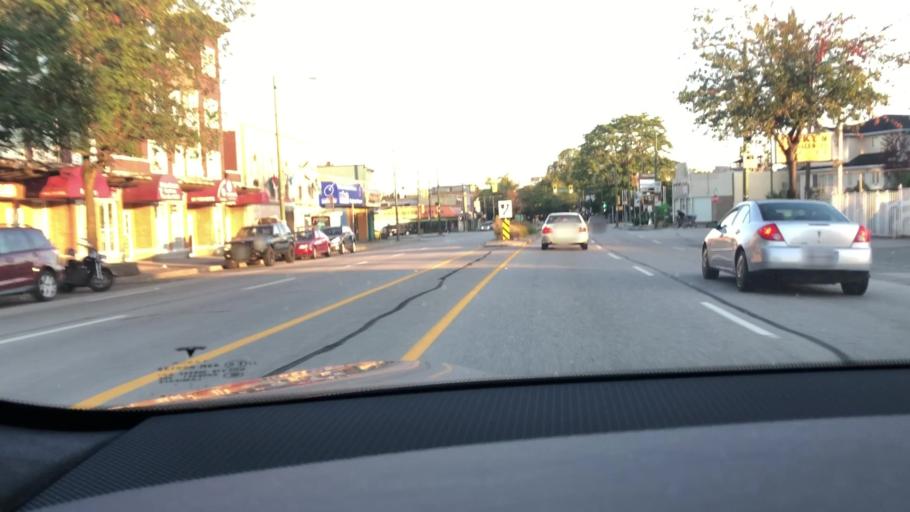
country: CA
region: British Columbia
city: Vancouver
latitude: 49.2561
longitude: -123.0884
